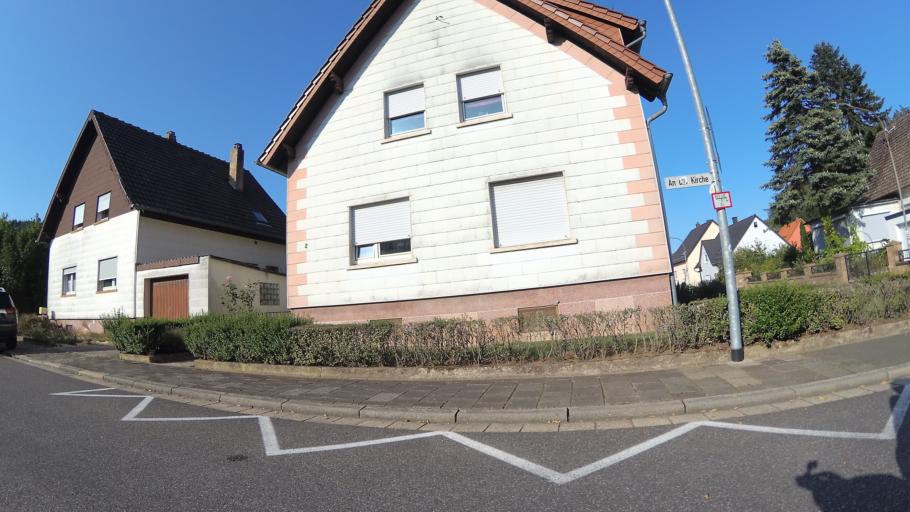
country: DE
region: Saarland
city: Blieskastel
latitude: 49.2370
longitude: 7.2350
